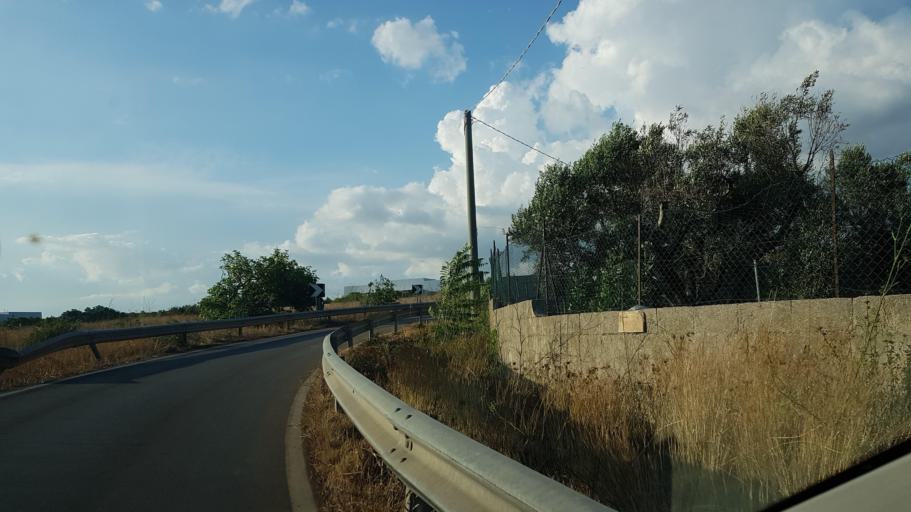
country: IT
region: Apulia
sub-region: Provincia di Lecce
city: Gemini
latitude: 39.8469
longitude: 18.2074
